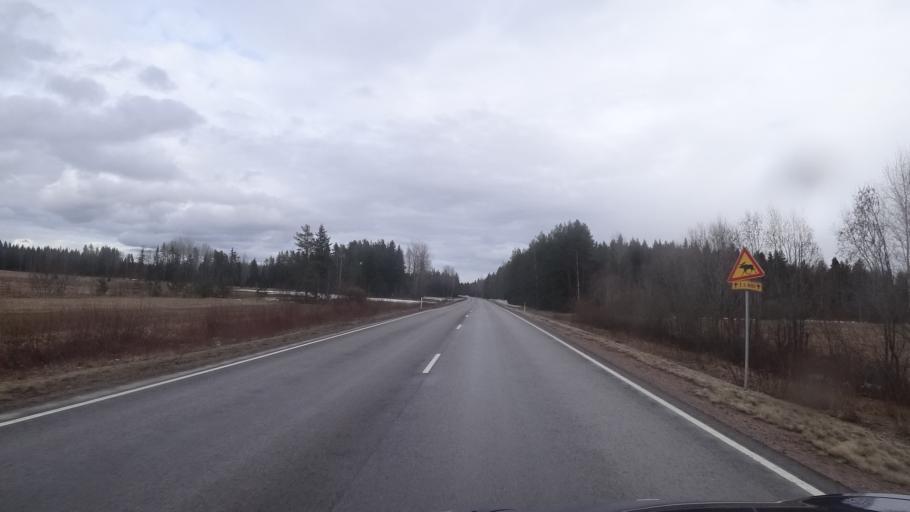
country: FI
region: Kymenlaakso
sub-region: Kouvola
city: Elimaeki
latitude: 60.6900
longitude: 26.6101
